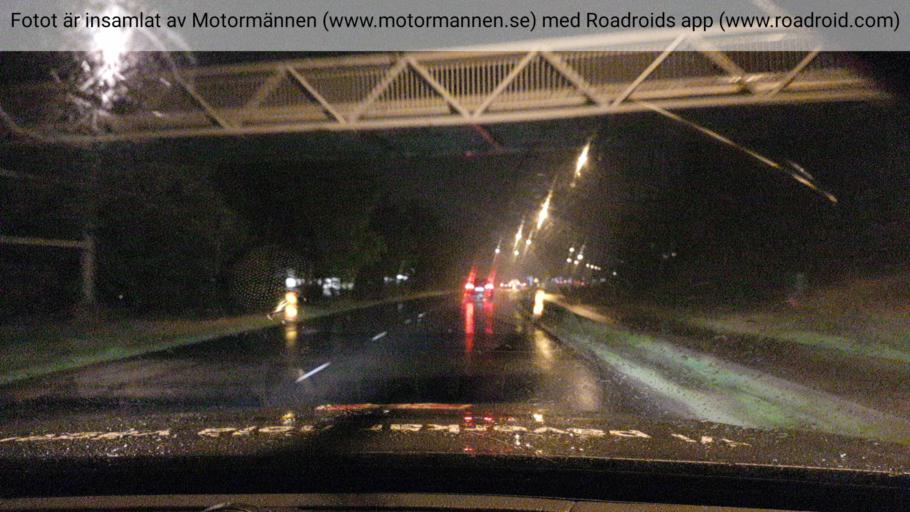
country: SE
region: Stockholm
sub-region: Haninge Kommun
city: Haninge
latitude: 59.1888
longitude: 18.1746
